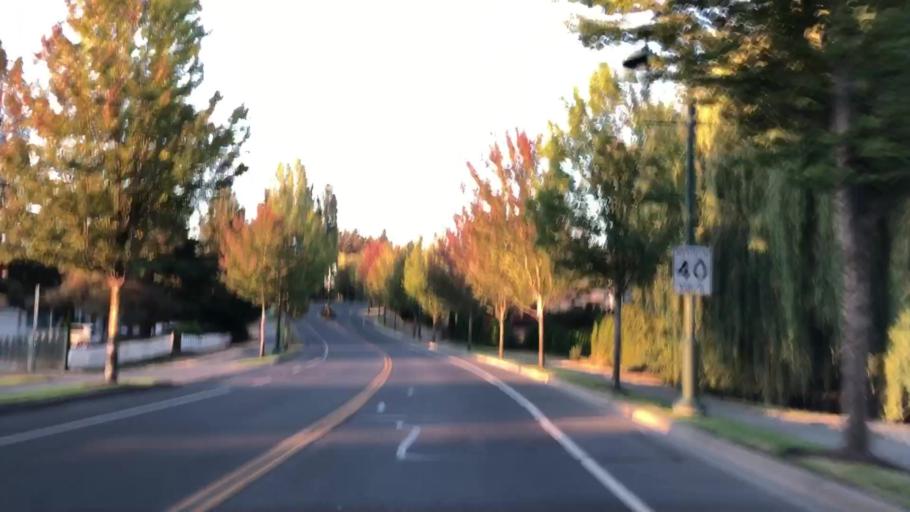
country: CA
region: British Columbia
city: Colwood
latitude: 48.4618
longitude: -123.4323
